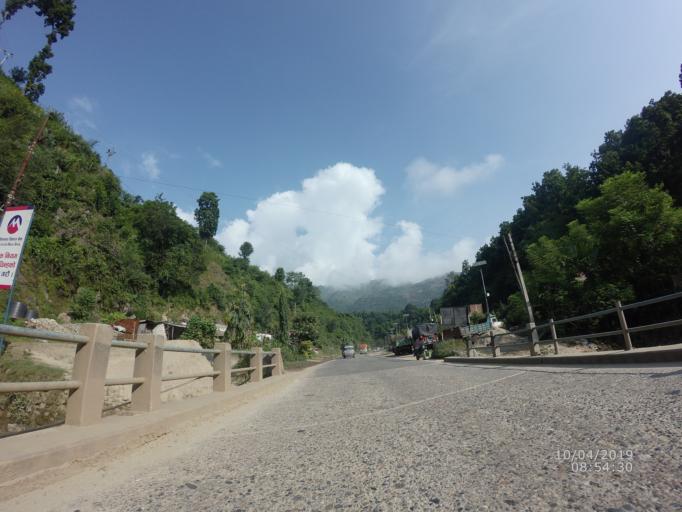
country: NP
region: Central Region
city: Kirtipur
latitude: 27.7975
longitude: 84.9943
